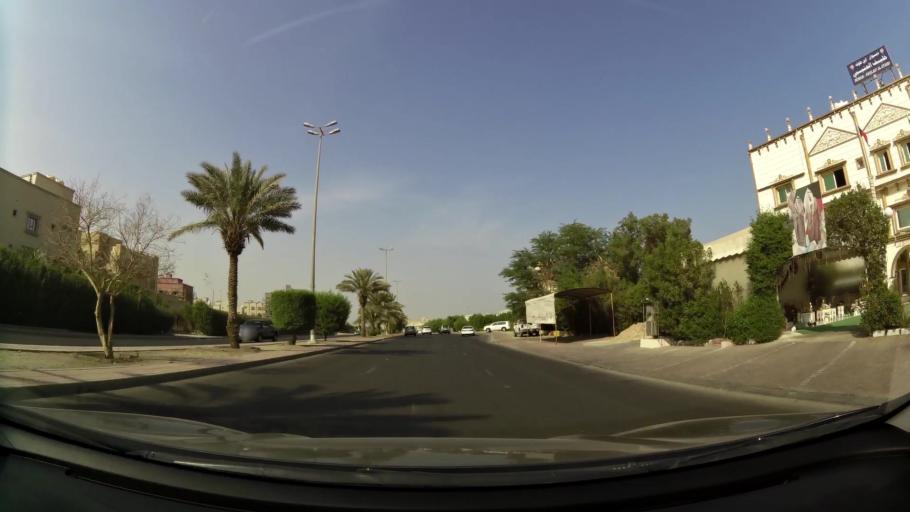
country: KW
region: Mubarak al Kabir
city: Mubarak al Kabir
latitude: 29.1672
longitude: 48.0857
